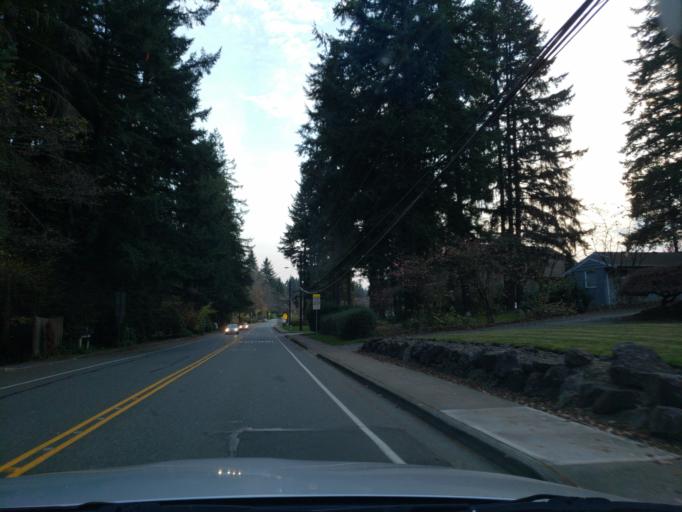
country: US
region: Washington
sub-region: King County
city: Bothell
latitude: 47.7634
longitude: -122.2176
